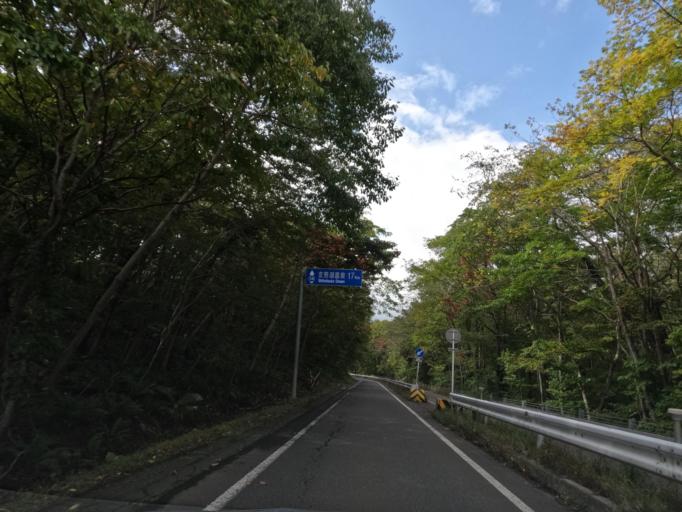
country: JP
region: Hokkaido
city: Chitose
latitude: 42.8026
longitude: 141.5761
